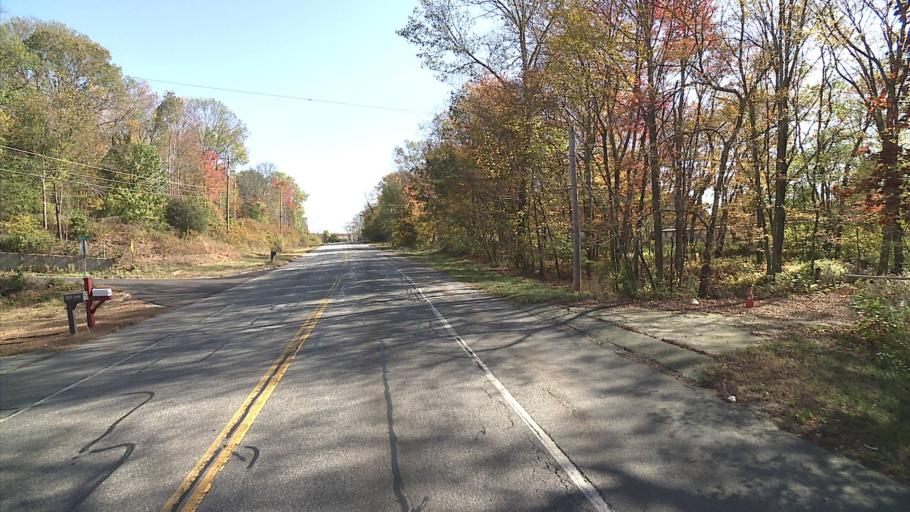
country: US
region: Connecticut
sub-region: Windham County
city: Windham
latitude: 41.7681
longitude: -72.0964
